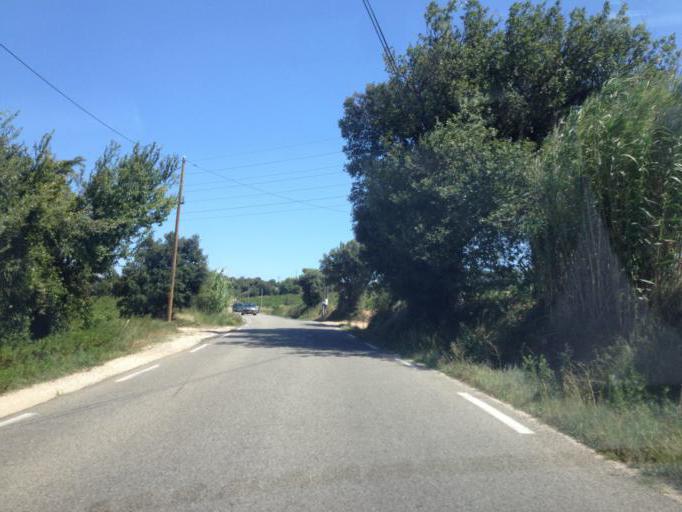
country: FR
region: Provence-Alpes-Cote d'Azur
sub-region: Departement du Vaucluse
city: Chateauneuf-du-Pape
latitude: 44.0955
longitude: 4.8188
